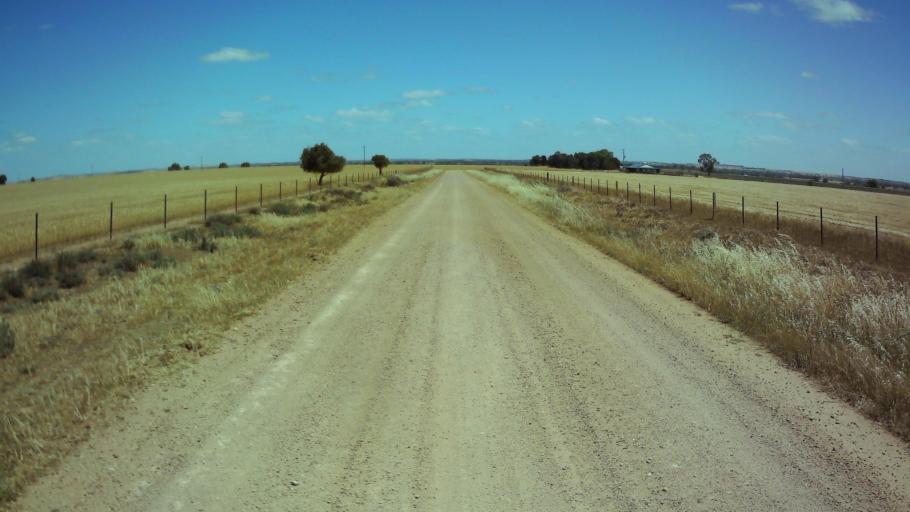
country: AU
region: New South Wales
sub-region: Weddin
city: Grenfell
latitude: -33.9682
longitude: 148.3299
